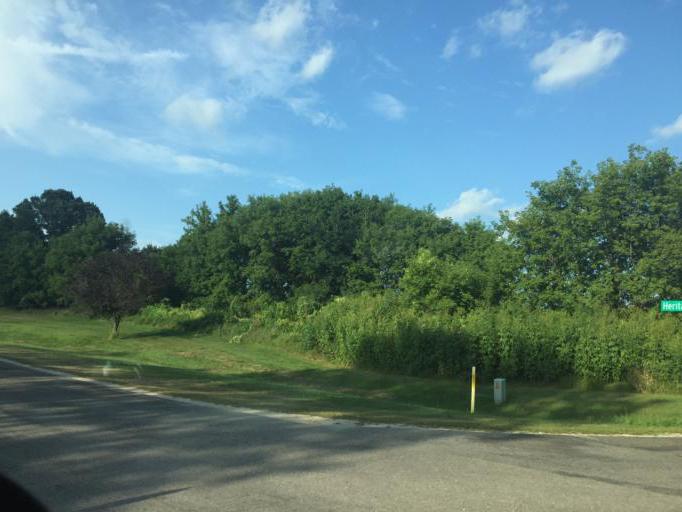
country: US
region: Minnesota
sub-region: Olmsted County
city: Rochester
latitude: 43.9641
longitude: -92.5387
